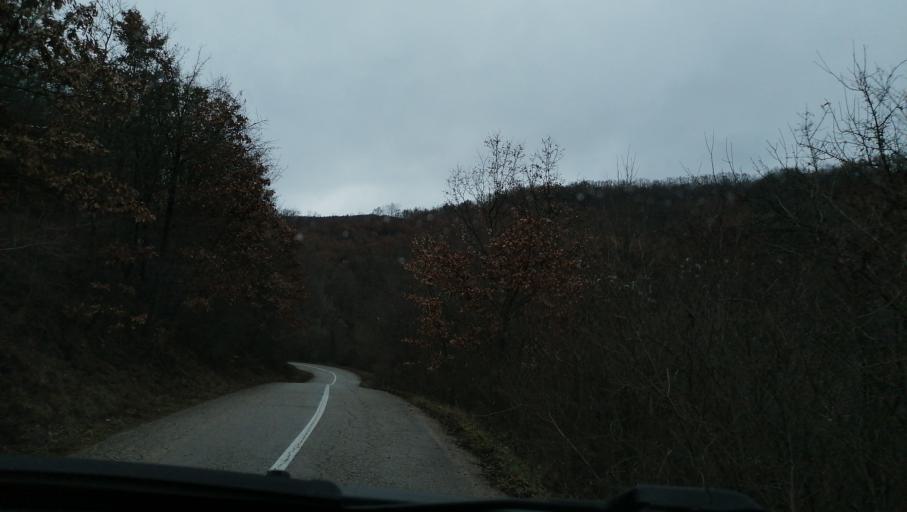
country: RS
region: Central Serbia
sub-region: Pirotski Okrug
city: Dimitrovgrad
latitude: 42.9749
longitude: 22.7849
